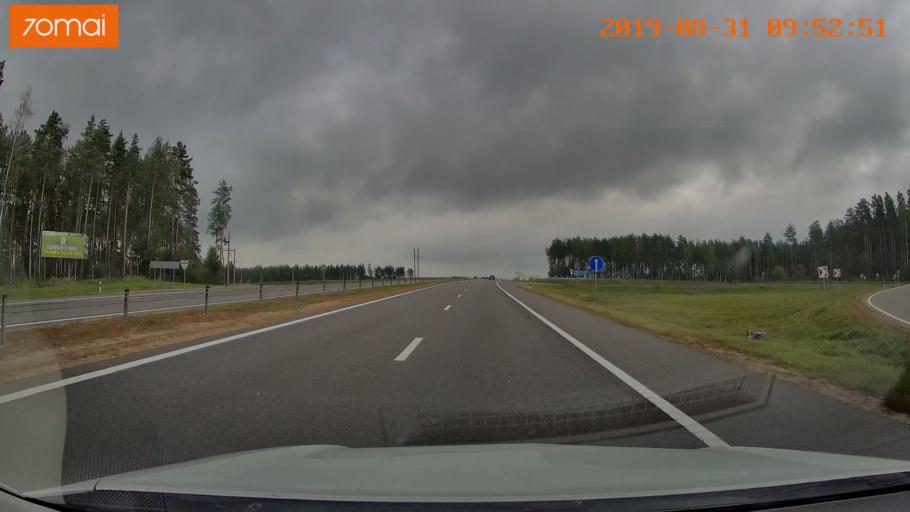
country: BY
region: Mogilev
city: Byalynichy
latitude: 53.9829
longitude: 29.7882
